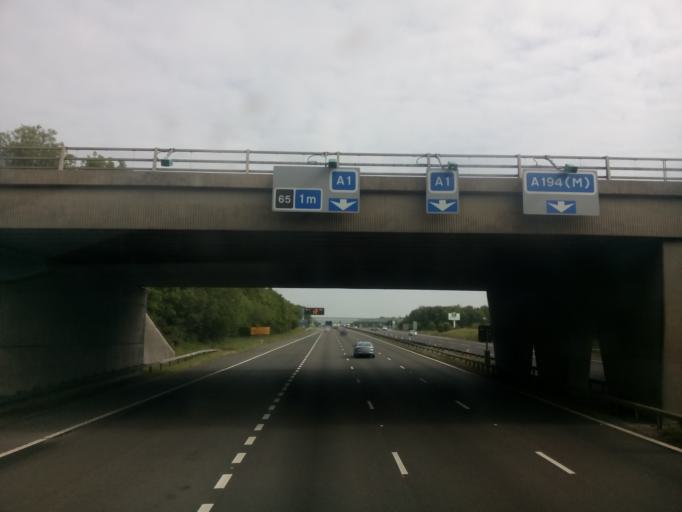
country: GB
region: England
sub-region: County Durham
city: Chester-le-Street
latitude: 54.8848
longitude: -1.5596
